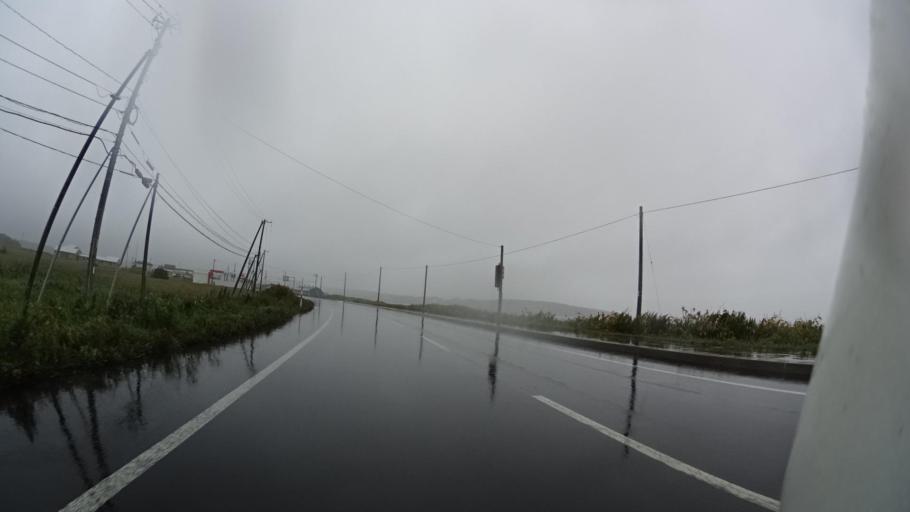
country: JP
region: Hokkaido
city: Nemuro
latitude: 43.2737
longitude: 145.4988
